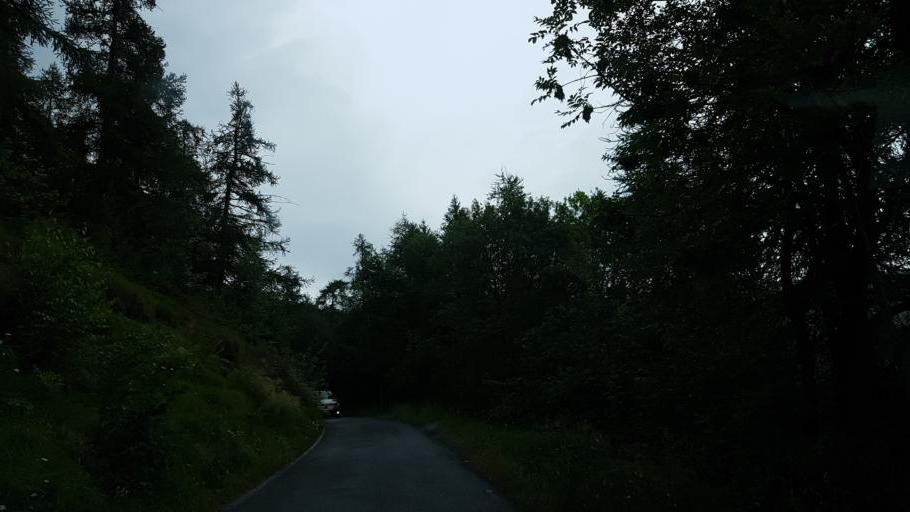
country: IT
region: Piedmont
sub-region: Provincia di Cuneo
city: Stroppo
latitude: 44.5103
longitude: 7.1102
